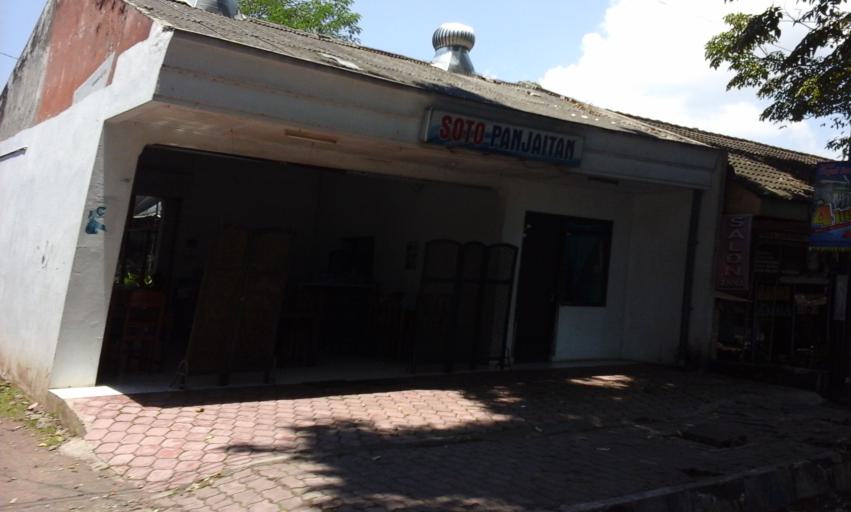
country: ID
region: East Java
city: Sumbersari Wetan
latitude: -8.1812
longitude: 113.7132
